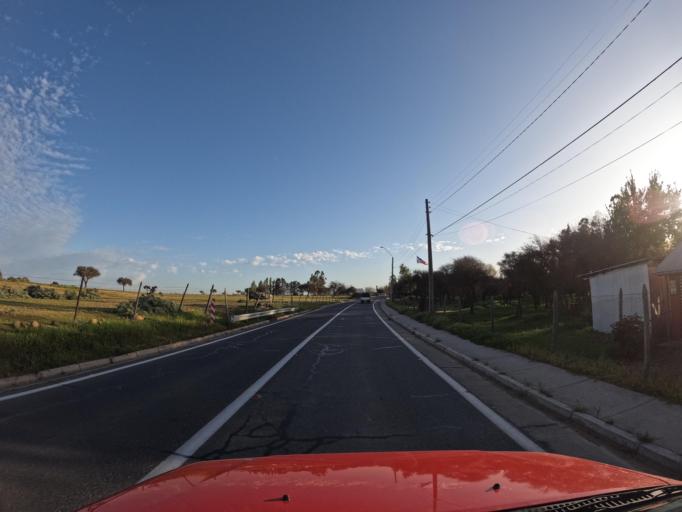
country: CL
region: O'Higgins
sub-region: Provincia de Colchagua
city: Santa Cruz
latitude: -34.2208
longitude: -71.7210
